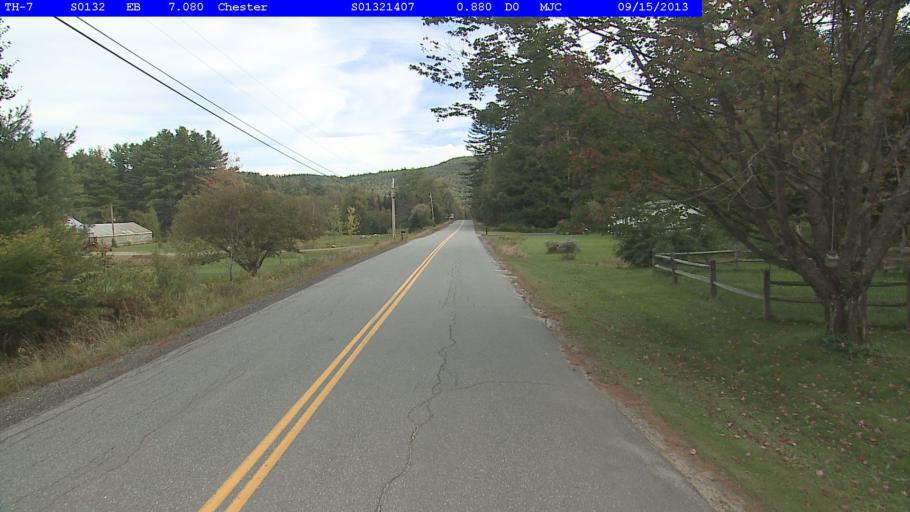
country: US
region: Vermont
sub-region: Windsor County
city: Chester
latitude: 43.2694
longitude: -72.6677
